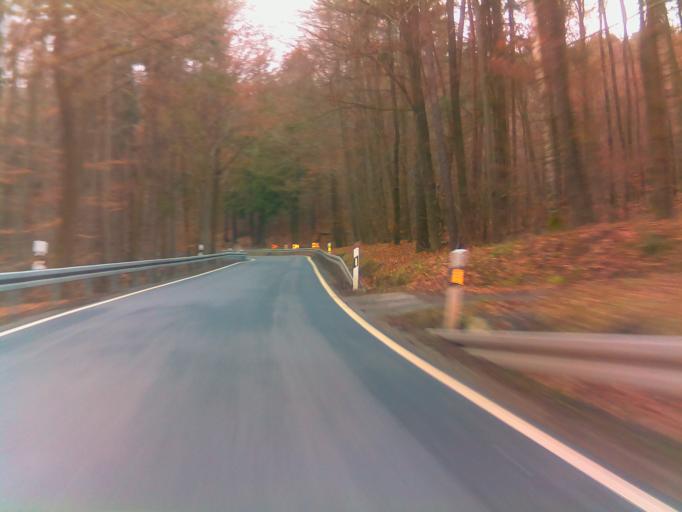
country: DE
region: Bavaria
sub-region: Regierungsbezirk Unterfranken
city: Miltenberg
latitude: 49.6881
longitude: 9.2931
